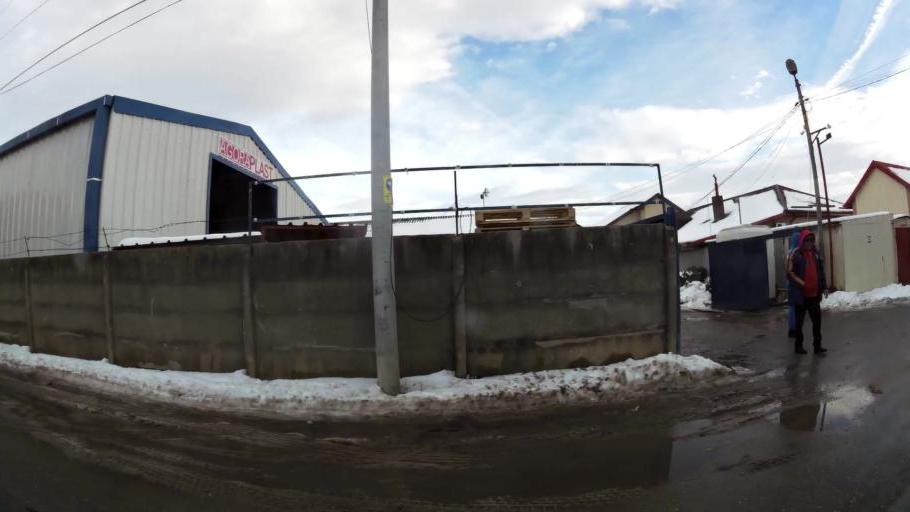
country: RO
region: Ilfov
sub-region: Comuna Fundeni-Dobroesti
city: Fundeni
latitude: 44.4577
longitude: 26.1753
